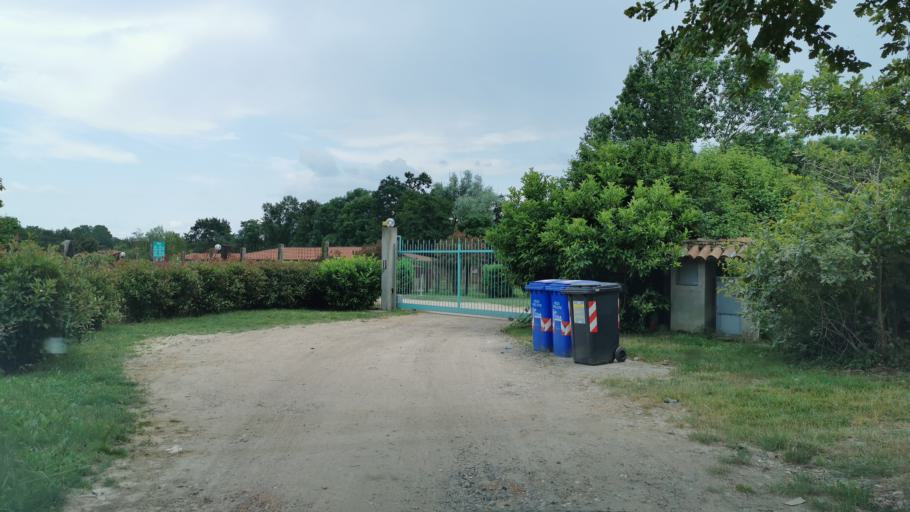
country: IT
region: Piedmont
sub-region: Provincia di Torino
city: Barbania
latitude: 45.3007
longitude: 7.6399
